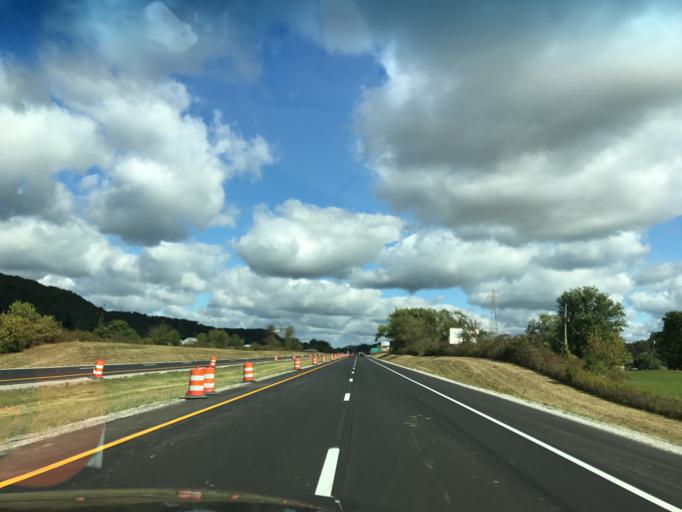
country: US
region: Ohio
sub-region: Fairfield County
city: Lancaster
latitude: 39.6127
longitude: -82.5499
